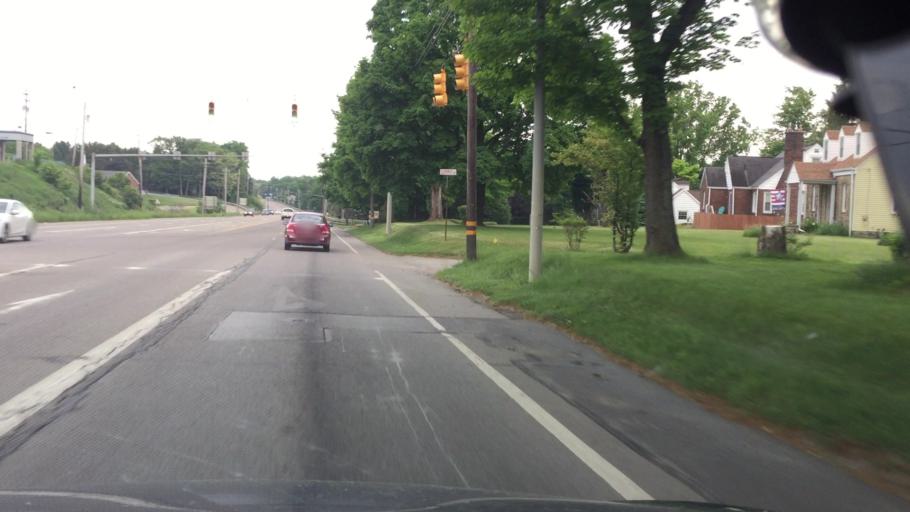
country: US
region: Pennsylvania
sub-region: Butler County
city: Shanor-Northvue
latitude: 40.8943
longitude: -79.9069
